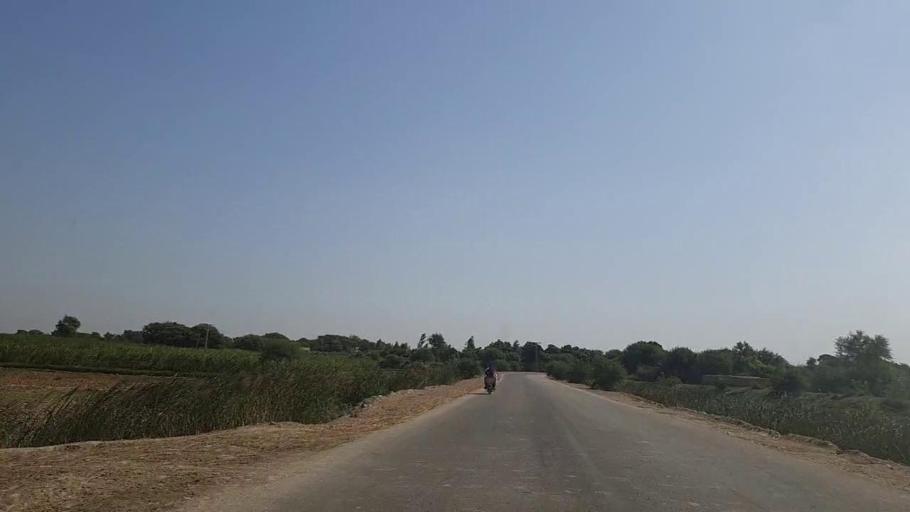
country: PK
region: Sindh
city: Daro Mehar
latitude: 24.7653
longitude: 68.2165
